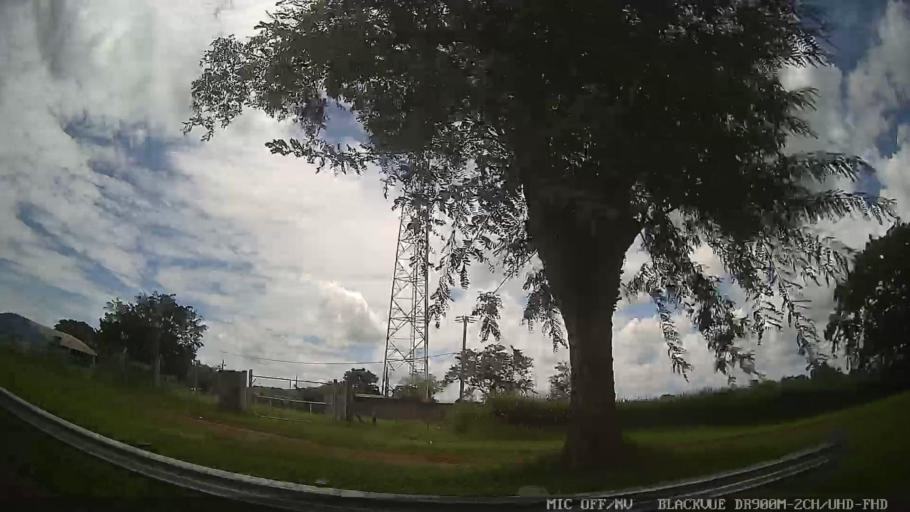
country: BR
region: Sao Paulo
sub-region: Laranjal Paulista
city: Laranjal Paulista
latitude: -23.0436
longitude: -47.9118
